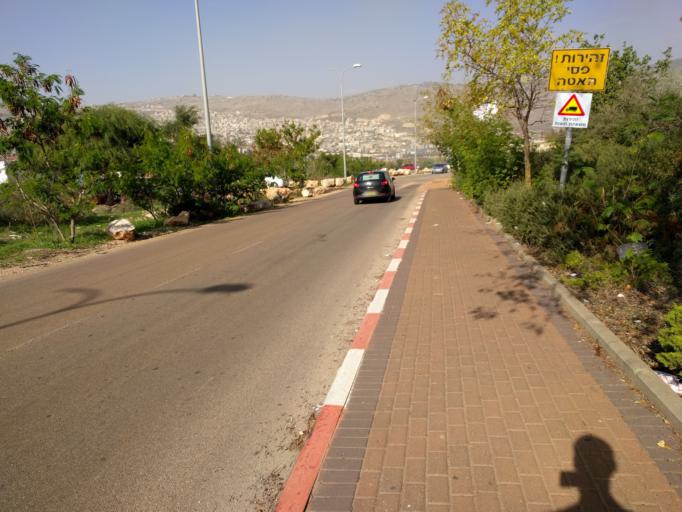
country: IL
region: Northern District
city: Karmi'el
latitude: 32.9114
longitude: 35.2804
